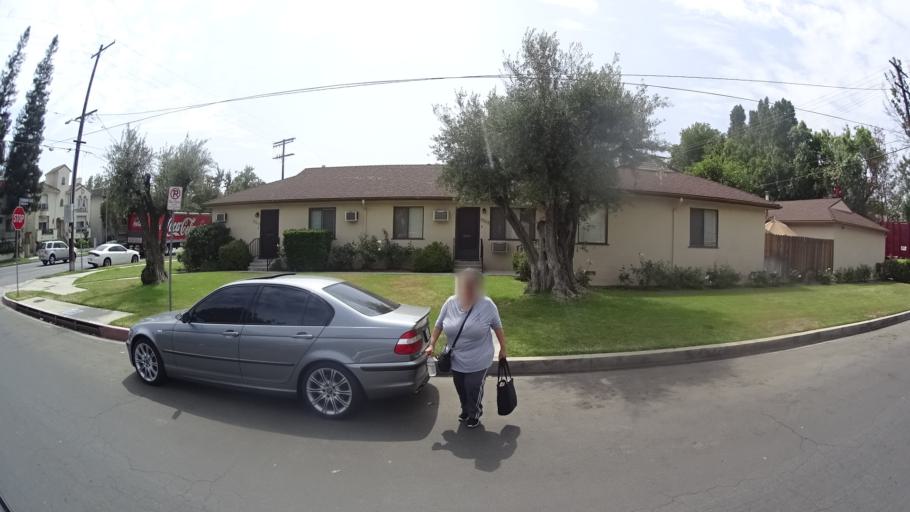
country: US
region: California
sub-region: Los Angeles County
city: Van Nuys
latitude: 34.1724
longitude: -118.4553
